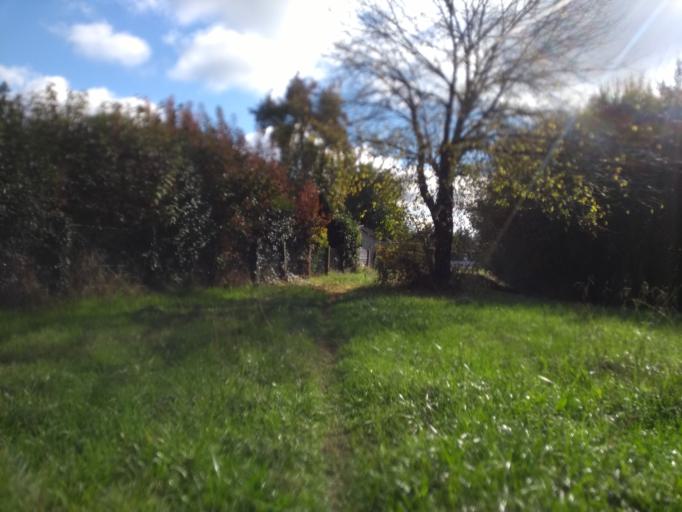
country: FR
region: Aquitaine
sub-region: Departement de la Gironde
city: Canejan
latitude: 44.7704
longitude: -0.6502
